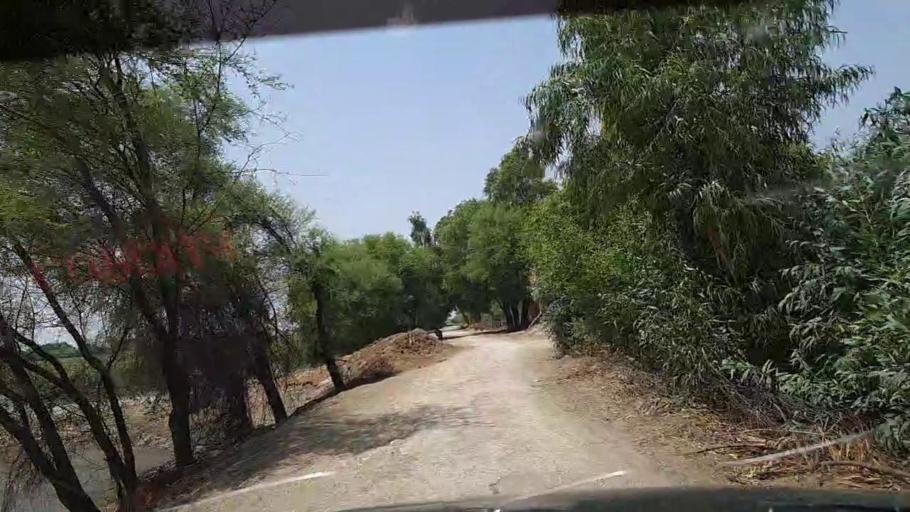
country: PK
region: Sindh
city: Ghotki
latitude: 28.0958
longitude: 69.3127
